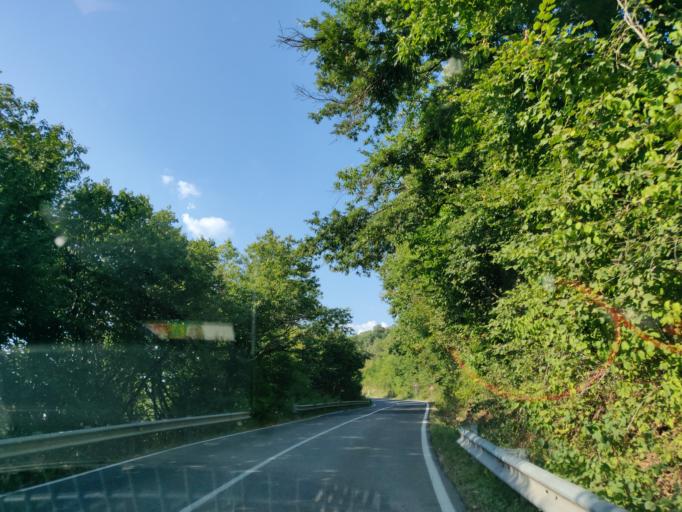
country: IT
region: Latium
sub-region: Provincia di Viterbo
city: Latera
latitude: 42.6166
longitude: 11.8395
